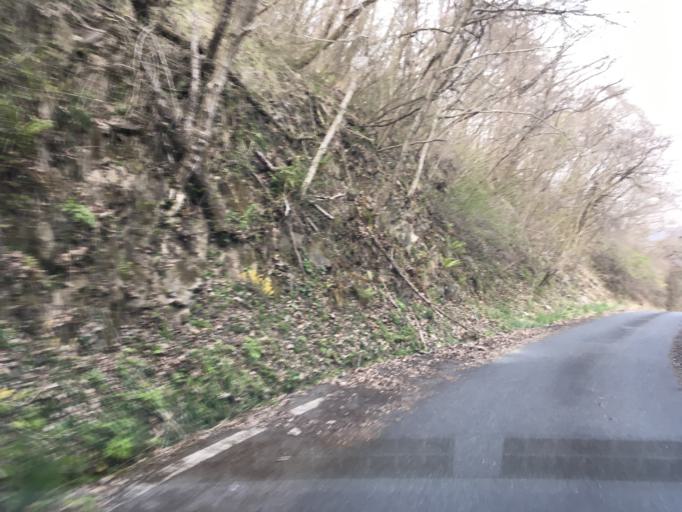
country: JP
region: Iwate
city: Ichinoseki
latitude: 38.9425
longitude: 141.2336
